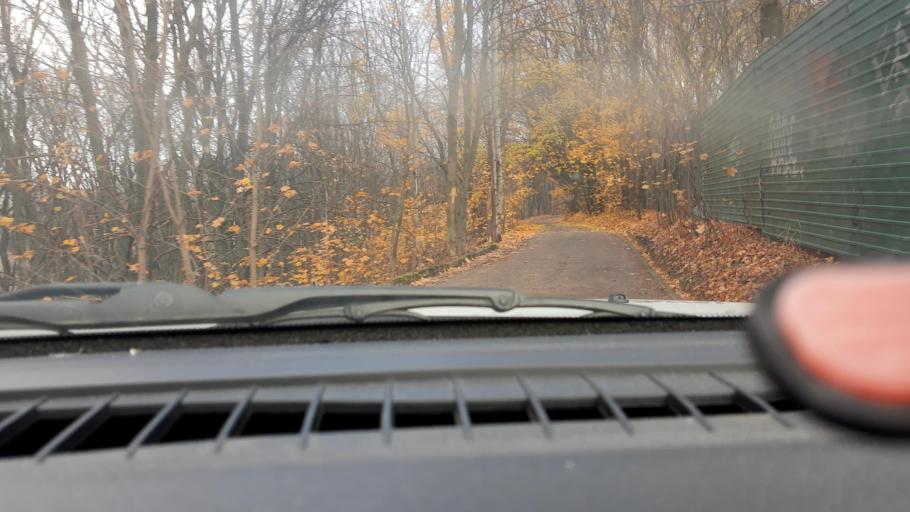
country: RU
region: Nizjnij Novgorod
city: Nizhniy Novgorod
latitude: 56.2972
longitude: 43.9715
